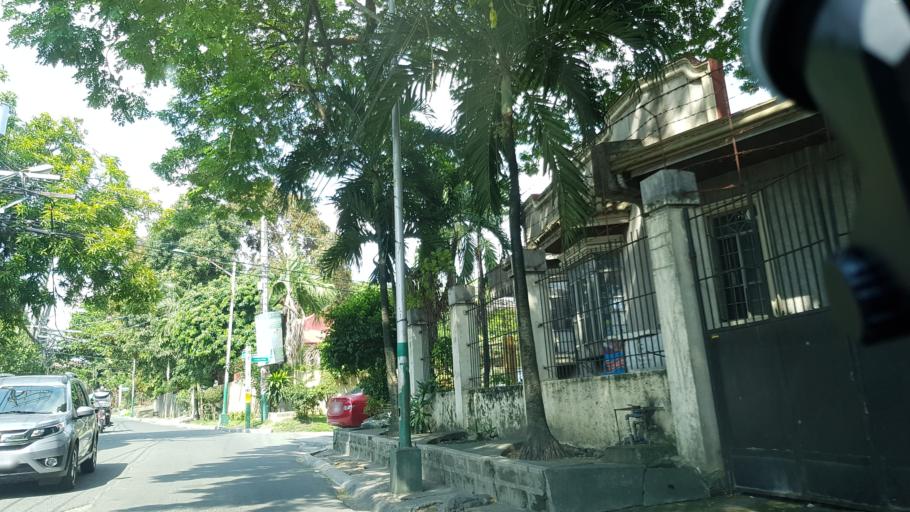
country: PH
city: Sambayanihan People's Village
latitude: 14.4728
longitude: 121.0244
